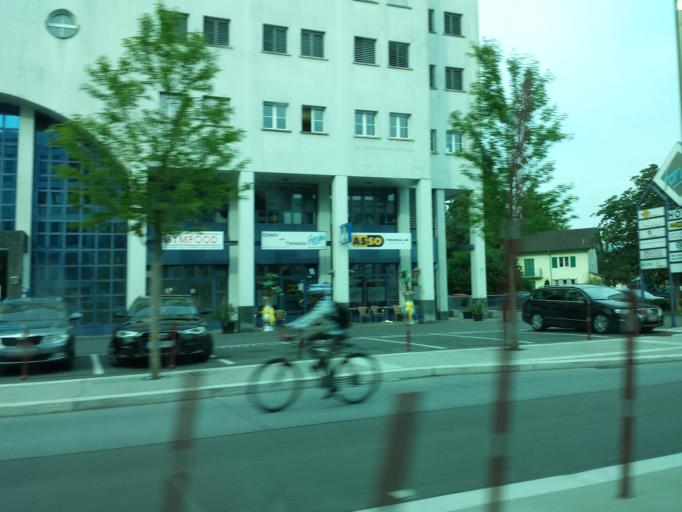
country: CH
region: Appenzell Innerrhoden
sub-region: Appenzell Inner Rhodes
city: Balgach
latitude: 47.4063
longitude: 9.6336
